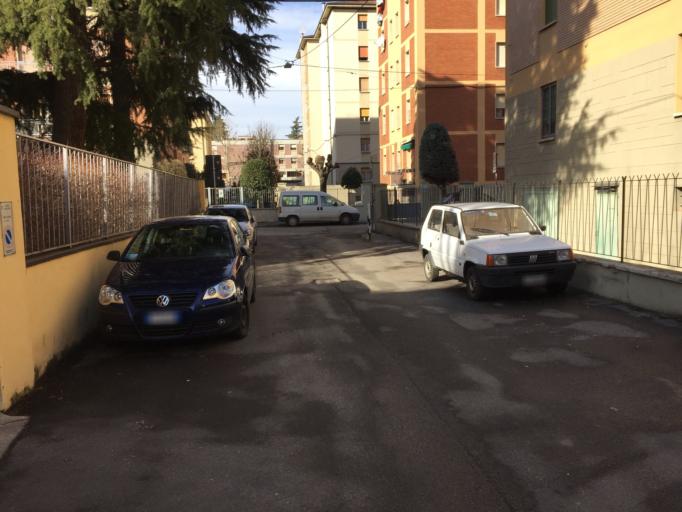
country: IT
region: Emilia-Romagna
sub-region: Provincia di Bologna
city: Calderara di Reno
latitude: 44.5199
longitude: 11.2729
